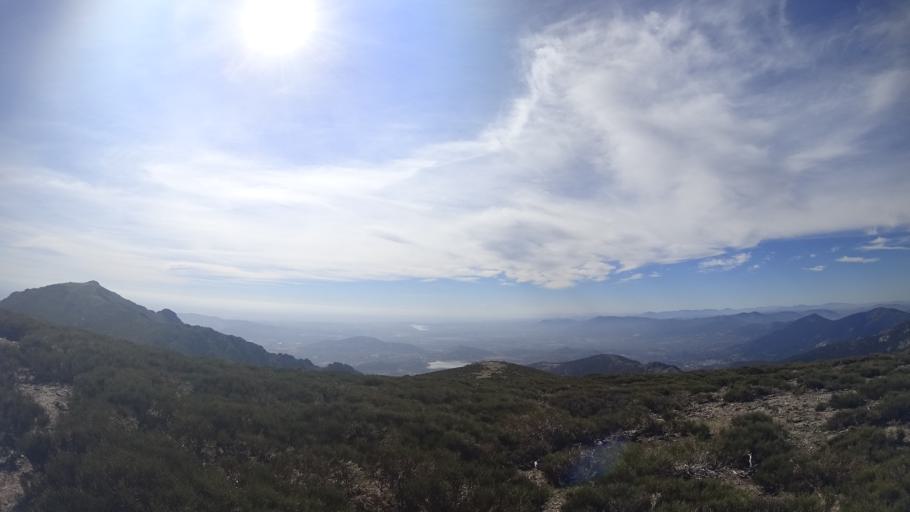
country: ES
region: Madrid
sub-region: Provincia de Madrid
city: Navacerrada
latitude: 40.7829
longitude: -3.9821
